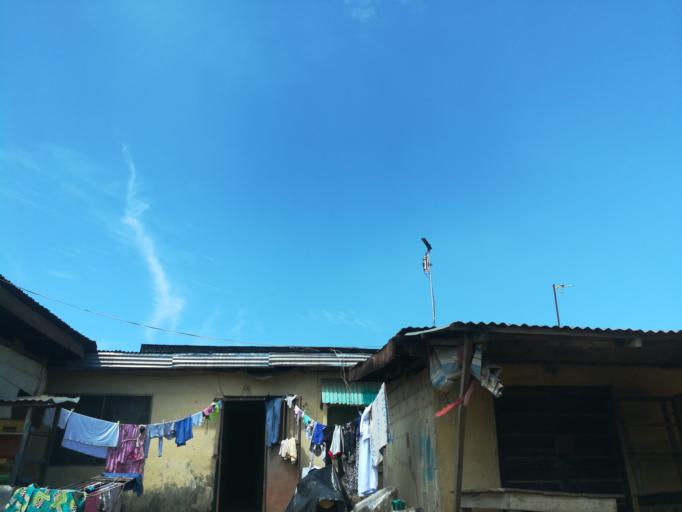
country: NG
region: Lagos
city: Oshodi
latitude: 6.5632
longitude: 3.3322
